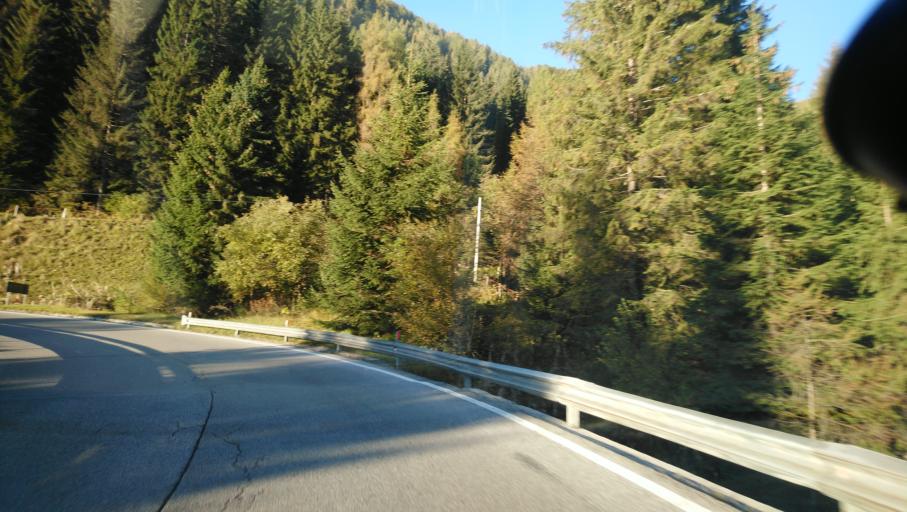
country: IT
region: Veneto
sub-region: Provincia di Belluno
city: Falcade Alto
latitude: 46.3600
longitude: 11.8474
